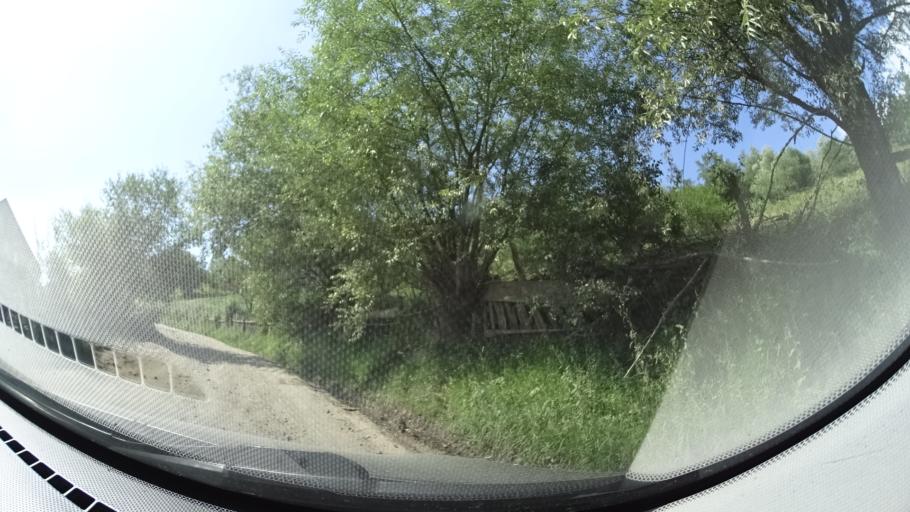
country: GE
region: Ajaria
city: Dioknisi
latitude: 41.6445
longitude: 42.4655
